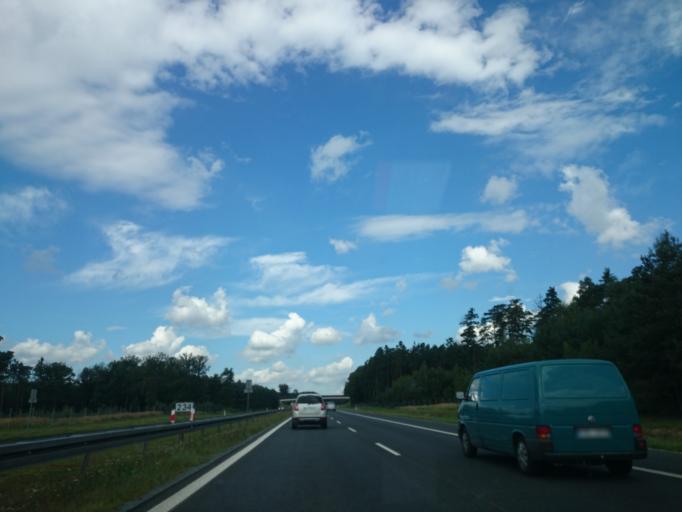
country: PL
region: Opole Voivodeship
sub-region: Powiat opolski
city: Komprachcice
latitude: 50.5905
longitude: 17.8103
